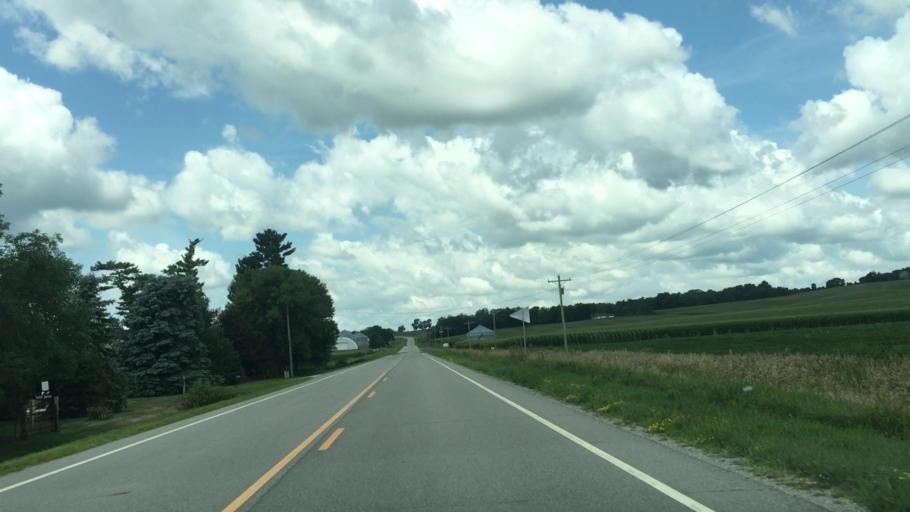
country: US
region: Iowa
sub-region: Linn County
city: Lisbon
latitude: 41.8410
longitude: -91.4018
